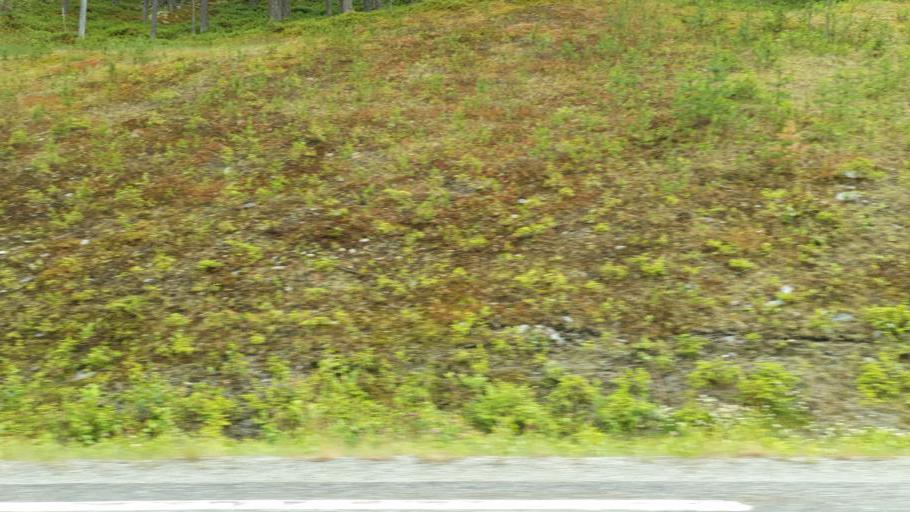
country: NO
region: Oppland
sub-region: Dovre
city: Dovre
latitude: 61.8499
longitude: 9.2970
